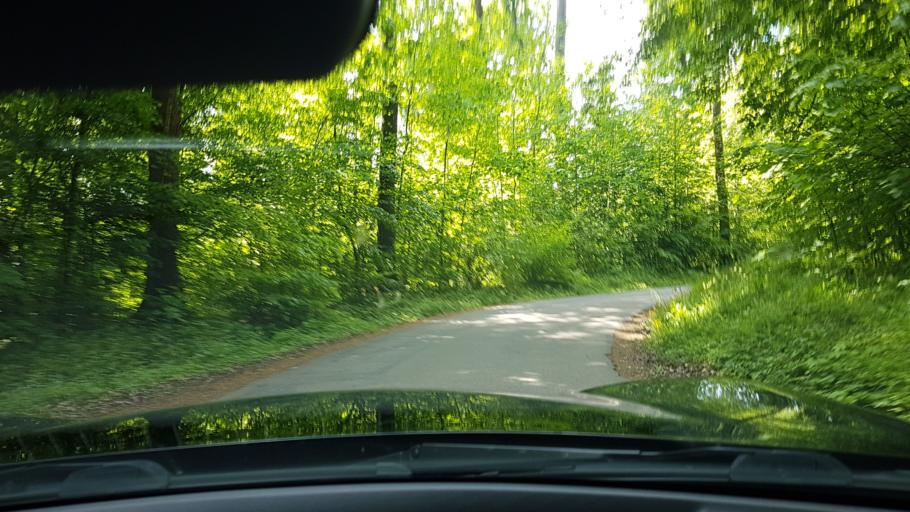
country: DE
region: Baden-Wuerttemberg
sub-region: Regierungsbezirk Stuttgart
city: Forchtenberg
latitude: 49.3120
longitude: 9.5716
